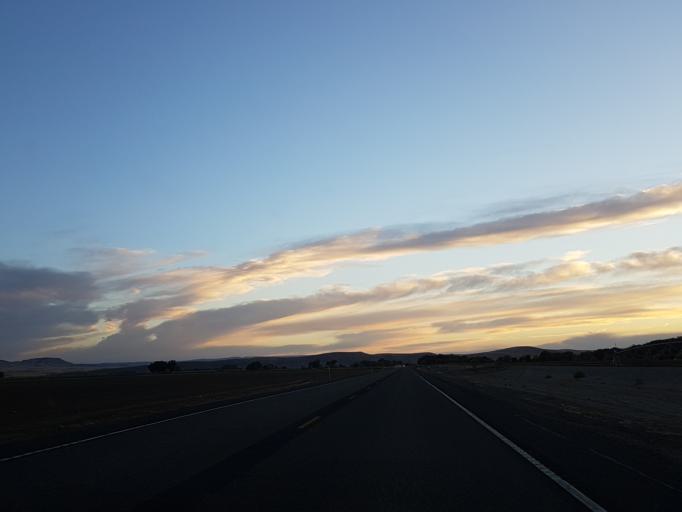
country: US
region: Oregon
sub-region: Malheur County
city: Vale
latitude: 43.9494
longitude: -117.2954
